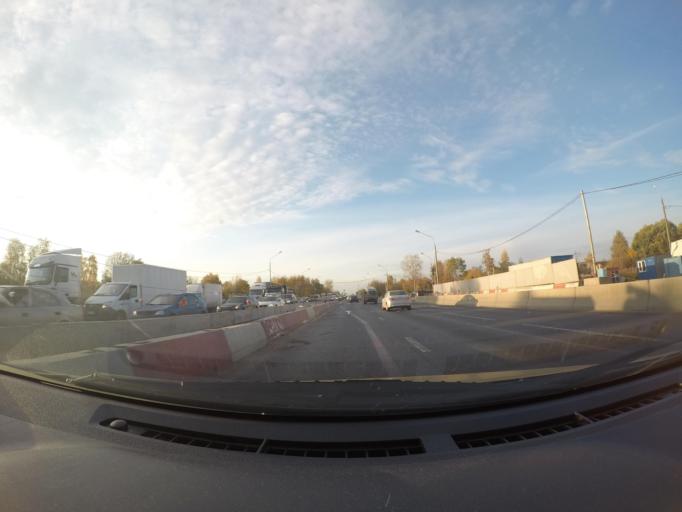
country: RU
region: Moscow
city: Khimki
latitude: 55.9216
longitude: 37.3915
